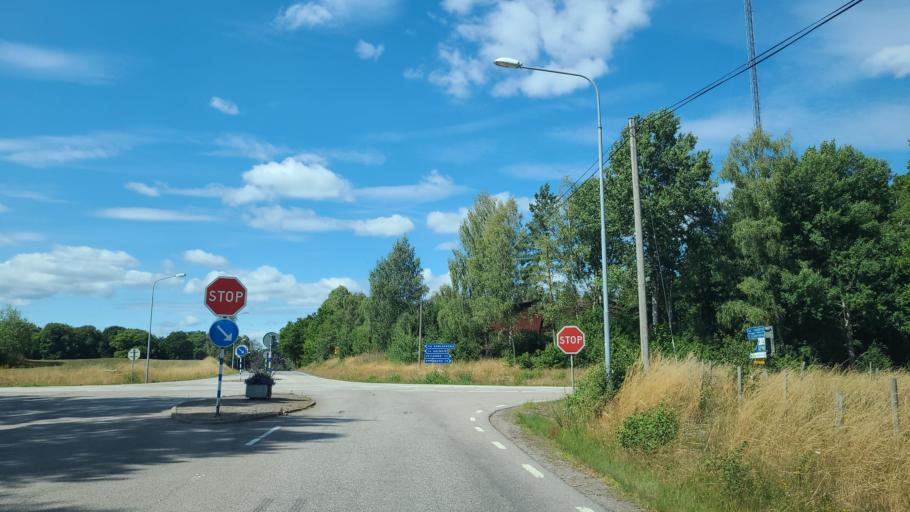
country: SE
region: Kalmar
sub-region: Emmaboda Kommun
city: Emmaboda
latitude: 56.5345
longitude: 15.6132
